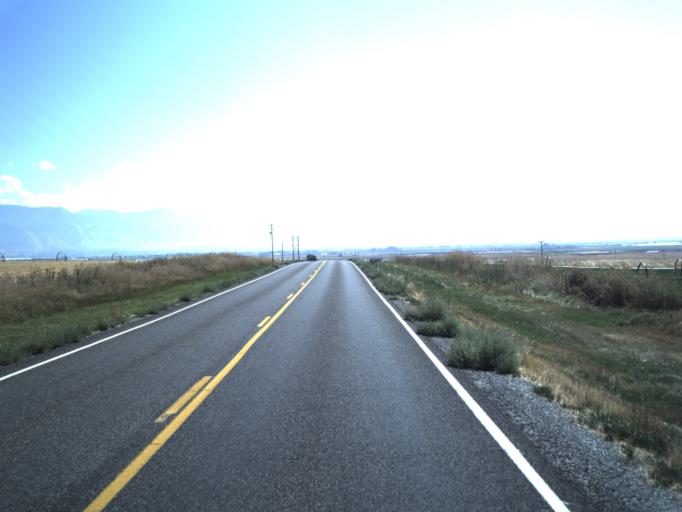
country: US
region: Utah
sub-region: Cache County
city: Benson
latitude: 41.8550
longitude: -111.9736
